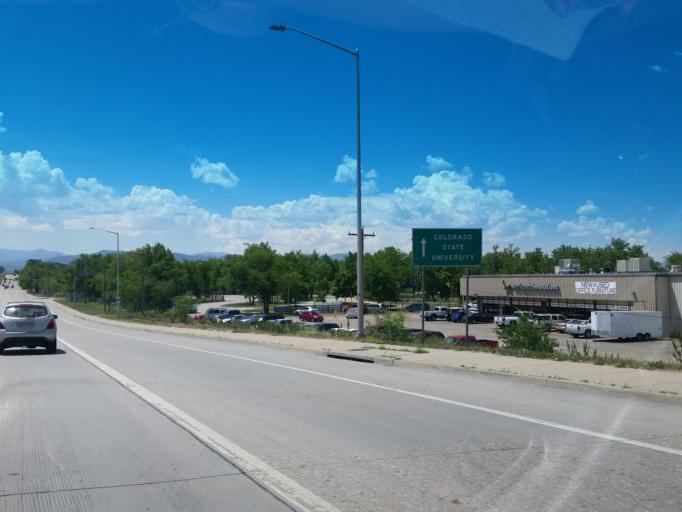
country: US
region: Colorado
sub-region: Weld County
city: Windsor
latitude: 40.5234
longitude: -104.9942
